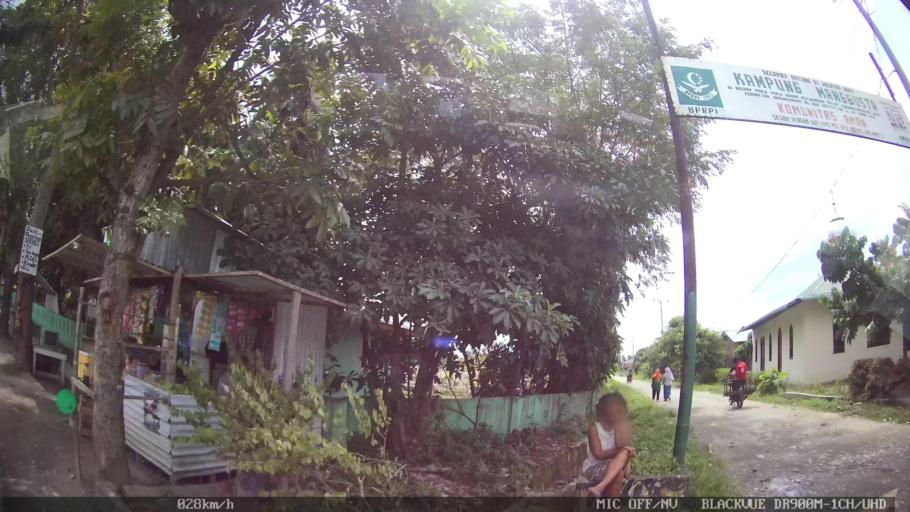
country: ID
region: North Sumatra
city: Sunggal
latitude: 3.6235
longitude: 98.6059
